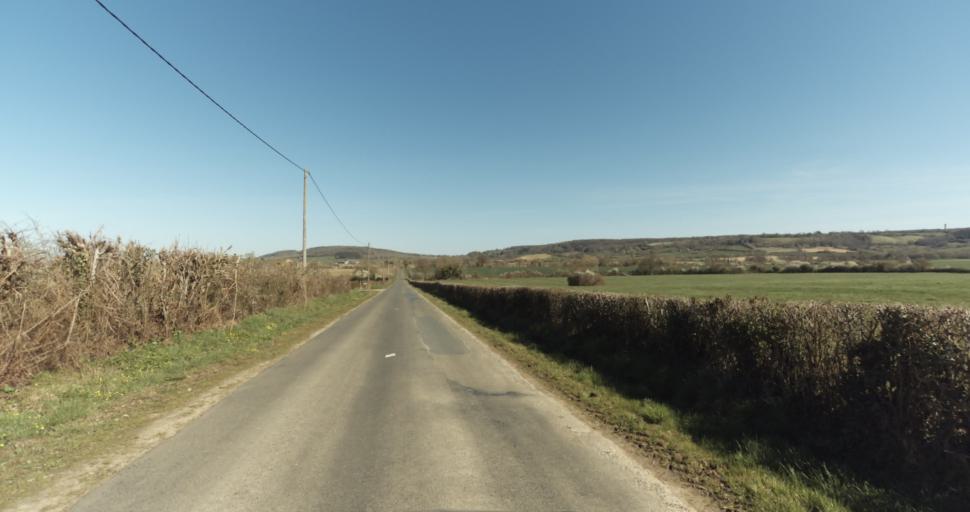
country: FR
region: Lower Normandy
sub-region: Departement du Calvados
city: Saint-Pierre-sur-Dives
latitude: 48.9543
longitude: 0.0492
